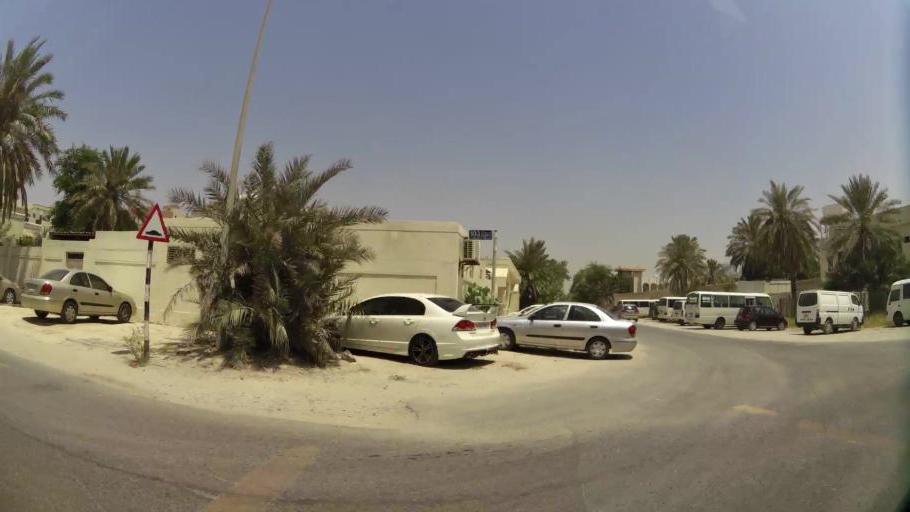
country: AE
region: Ajman
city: Ajman
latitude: 25.4035
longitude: 55.4338
